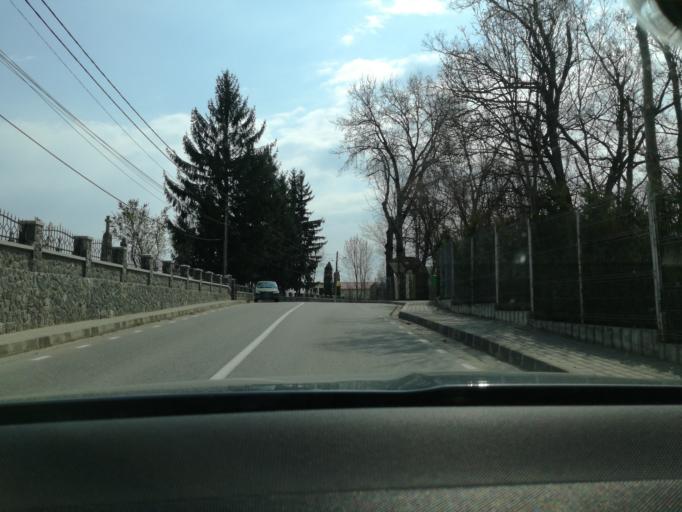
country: RO
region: Prahova
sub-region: Comuna Cornu
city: Cornu de Jos
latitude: 45.1512
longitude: 25.7054
